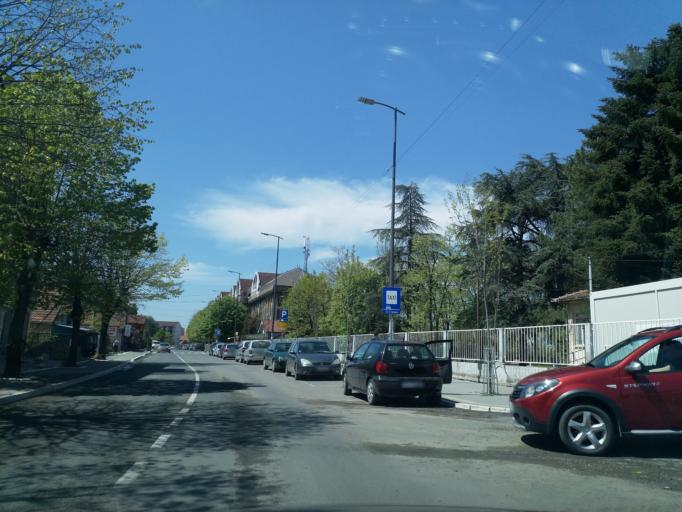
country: RS
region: Central Serbia
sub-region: Belgrade
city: Lazarevac
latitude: 44.3816
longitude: 20.2752
